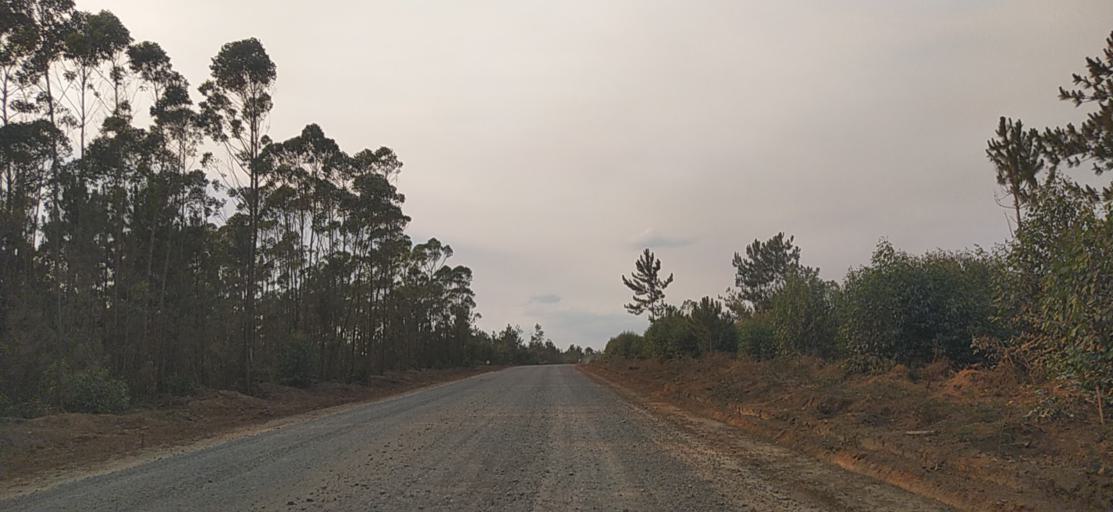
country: MG
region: Alaotra Mangoro
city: Moramanga
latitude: -18.5592
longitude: 48.2594
